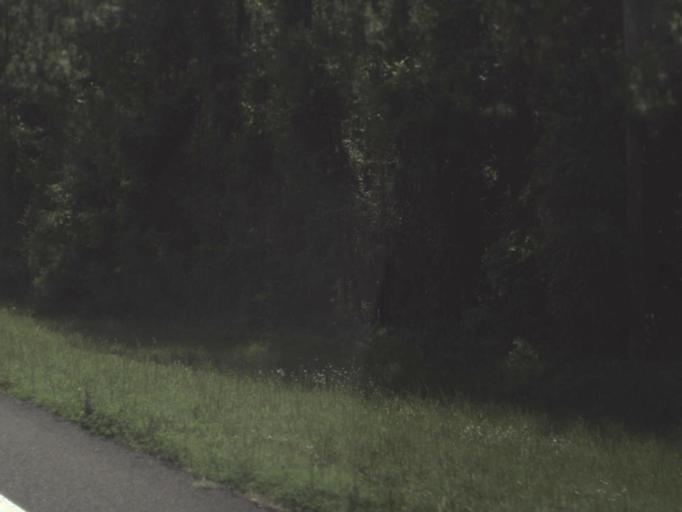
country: US
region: Florida
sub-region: Nassau County
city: Yulee
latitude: 30.5627
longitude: -81.6176
